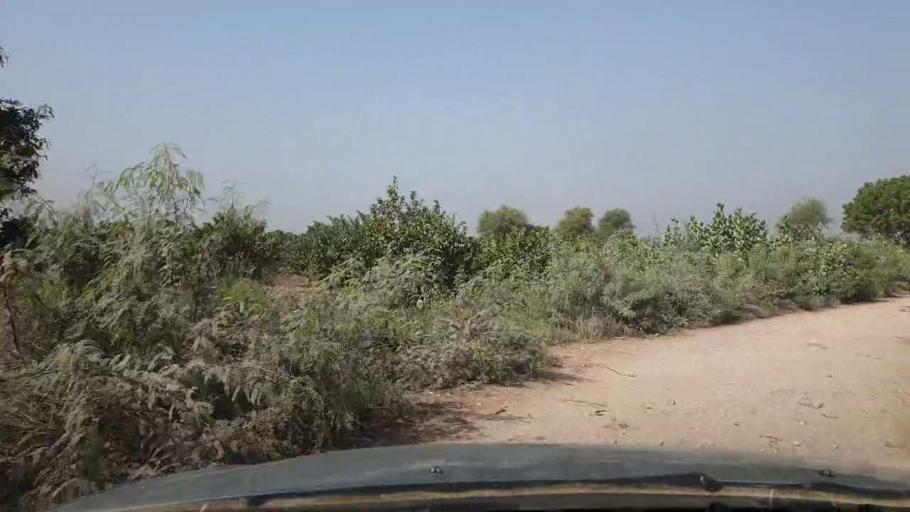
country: PK
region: Sindh
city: Tando Jam
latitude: 25.3704
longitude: 68.5326
